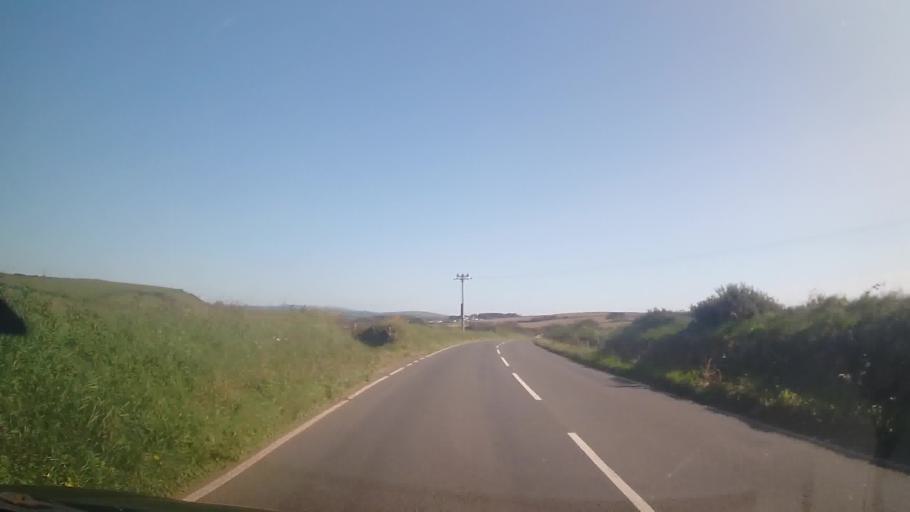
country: GB
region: Wales
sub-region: Pembrokeshire
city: Mathry
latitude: 51.9446
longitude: -5.0746
